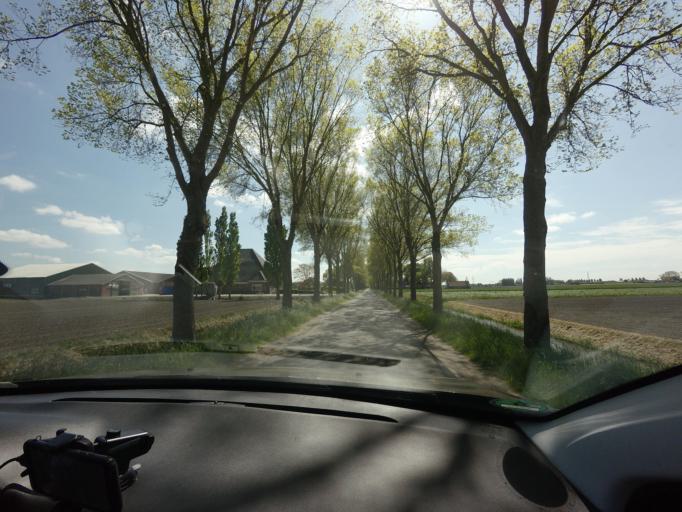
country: NL
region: North Holland
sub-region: Gemeente Beemster
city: Halfweg
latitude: 52.5711
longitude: 4.8776
